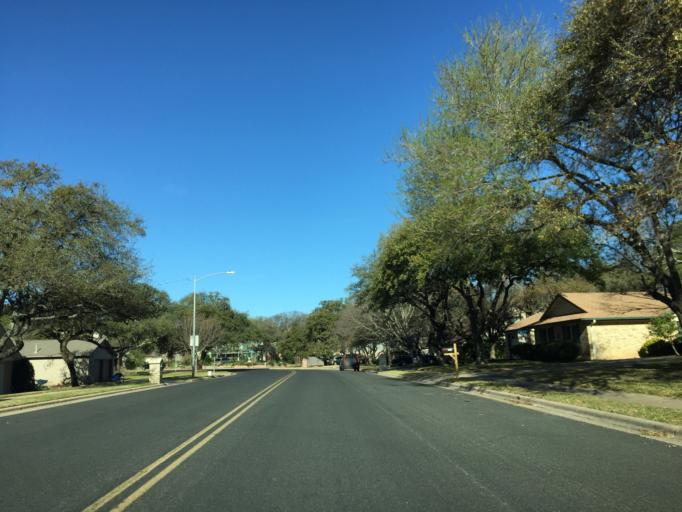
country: US
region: Texas
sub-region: Williamson County
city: Jollyville
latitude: 30.4058
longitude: -97.7316
